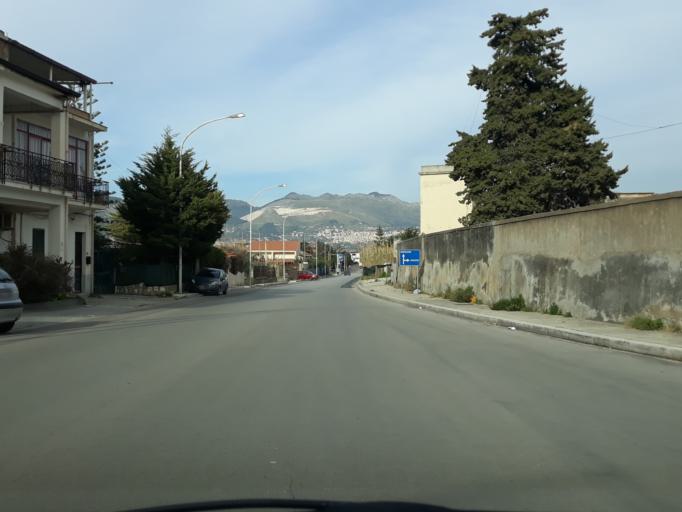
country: IT
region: Sicily
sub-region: Palermo
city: Partinico
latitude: 38.0543
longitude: 13.1283
